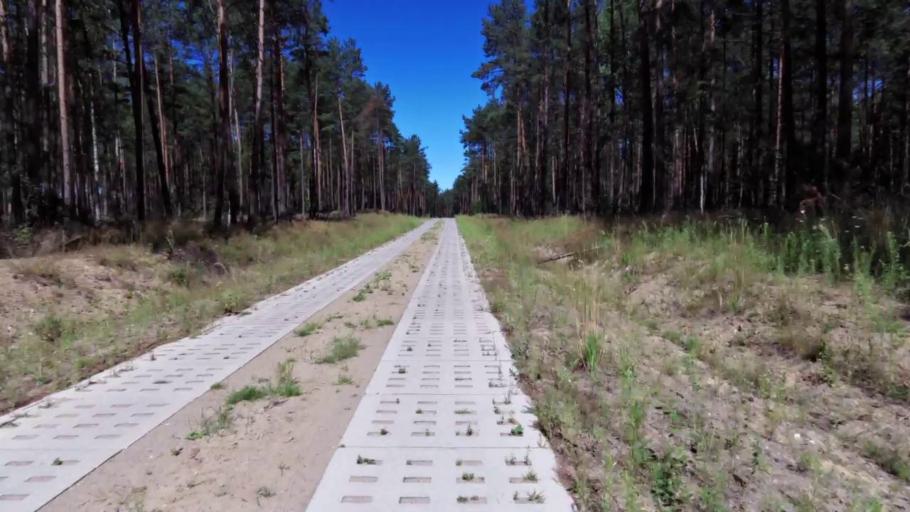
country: PL
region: West Pomeranian Voivodeship
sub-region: Powiat szczecinecki
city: Szczecinek
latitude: 53.6236
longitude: 16.6616
